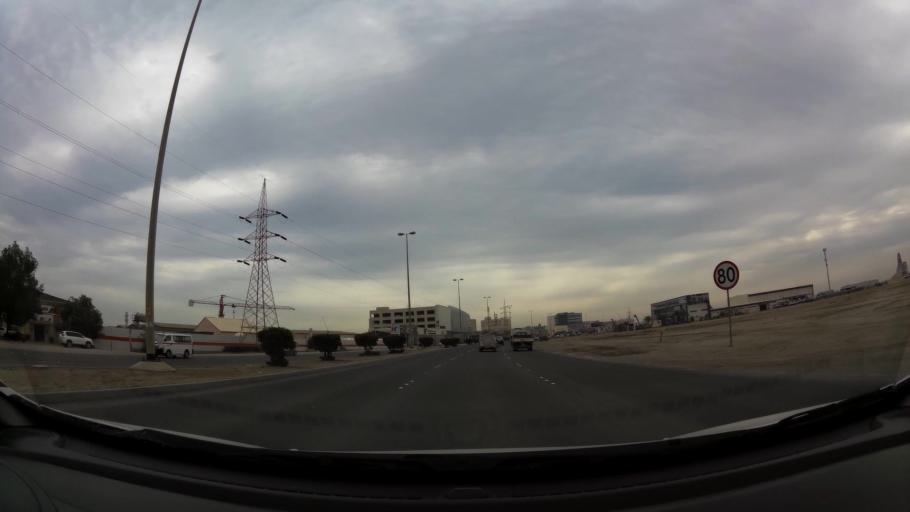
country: BH
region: Northern
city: Sitrah
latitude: 26.1531
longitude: 50.6149
